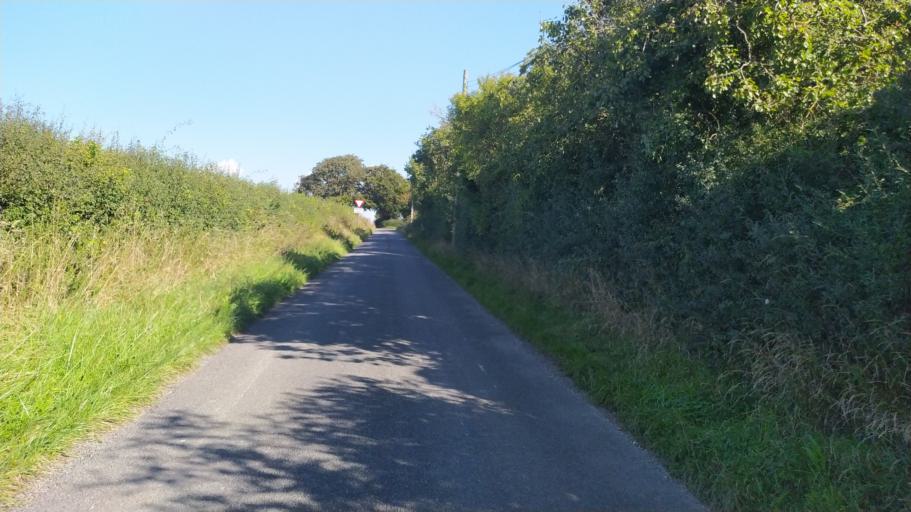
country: GB
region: England
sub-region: Hampshire
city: Abbotts Ann
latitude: 51.1648
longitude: -1.6037
